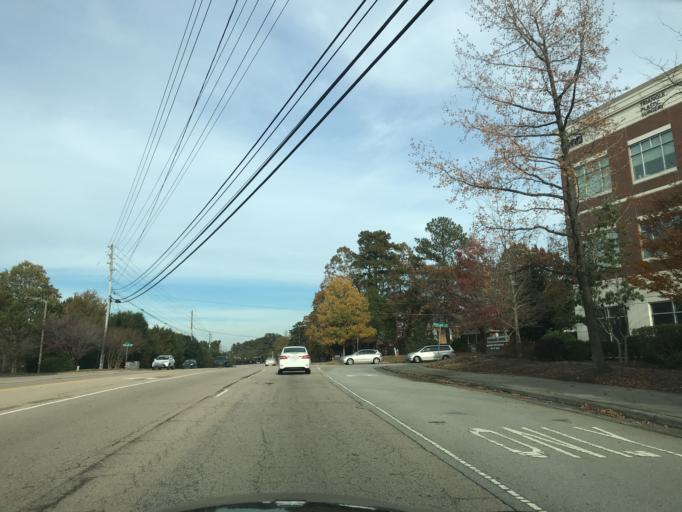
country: US
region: North Carolina
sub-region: Wake County
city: Wake Forest
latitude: 35.8999
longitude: -78.6074
